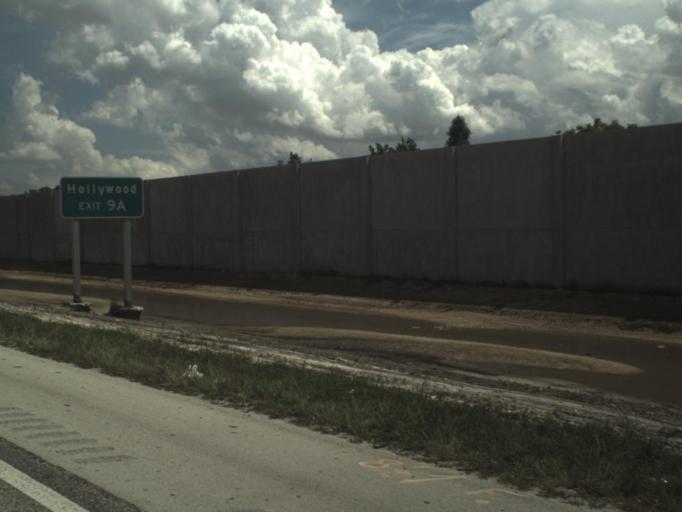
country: US
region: Florida
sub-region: Broward County
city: Sunshine Ranches
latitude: 26.0145
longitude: -80.3443
